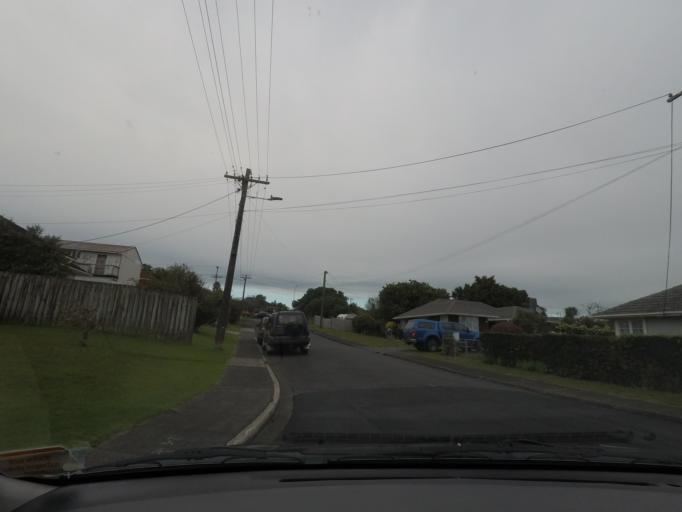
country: NZ
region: Auckland
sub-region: Auckland
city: Rosebank
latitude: -36.8624
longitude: 174.6443
